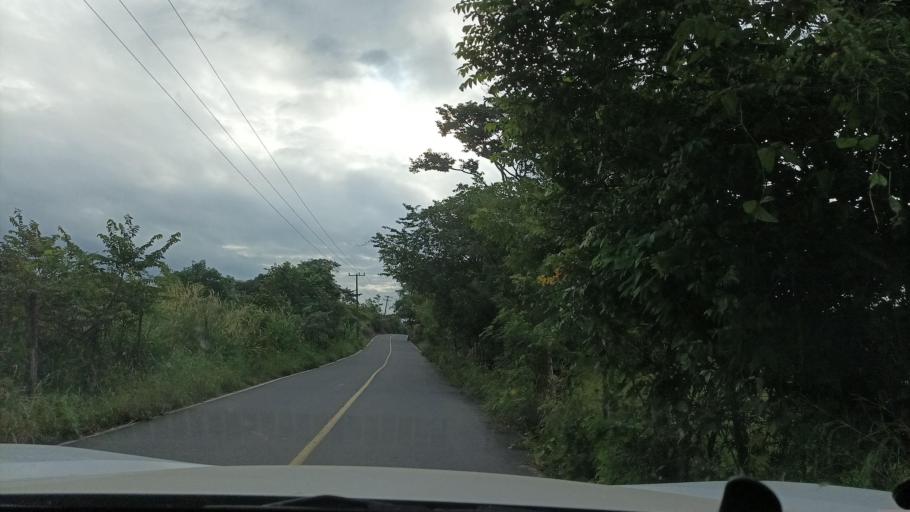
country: MX
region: Veracruz
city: Hidalgotitlan
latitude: 17.7158
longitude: -94.4741
